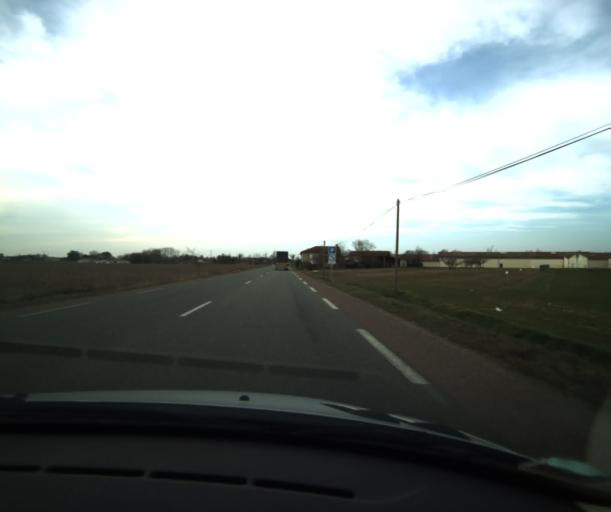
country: FR
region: Midi-Pyrenees
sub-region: Departement du Tarn-et-Garonne
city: Saint-Porquier
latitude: 43.9945
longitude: 1.1886
